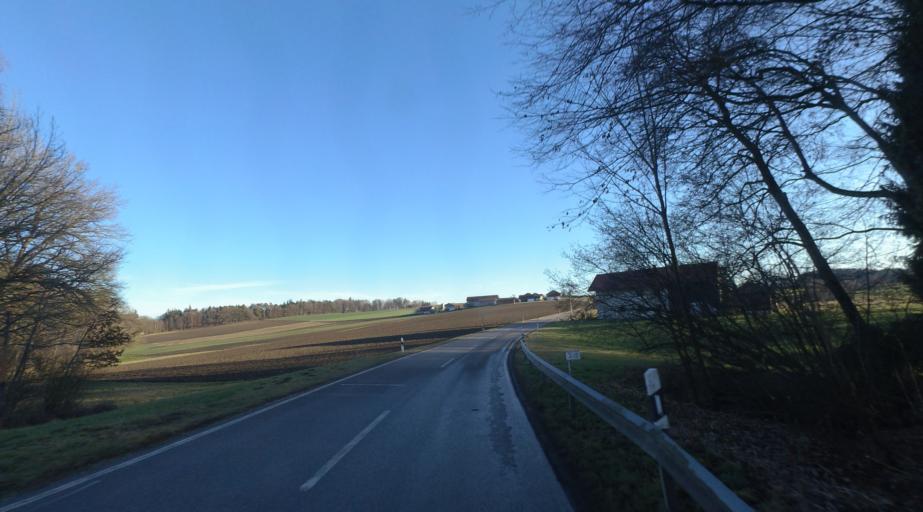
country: DE
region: Bavaria
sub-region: Upper Bavaria
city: Taching am See
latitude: 47.9863
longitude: 12.7704
